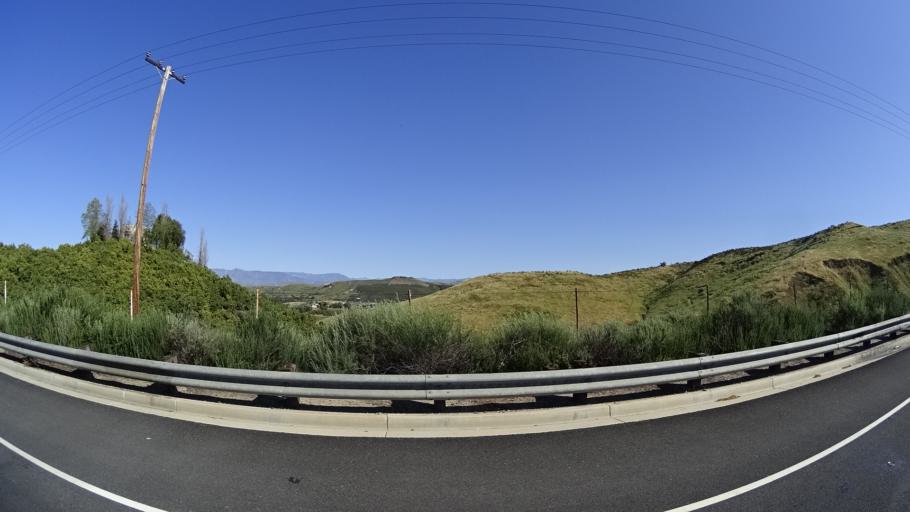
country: US
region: California
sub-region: Ventura County
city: Simi Valley
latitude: 34.2498
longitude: -118.8305
